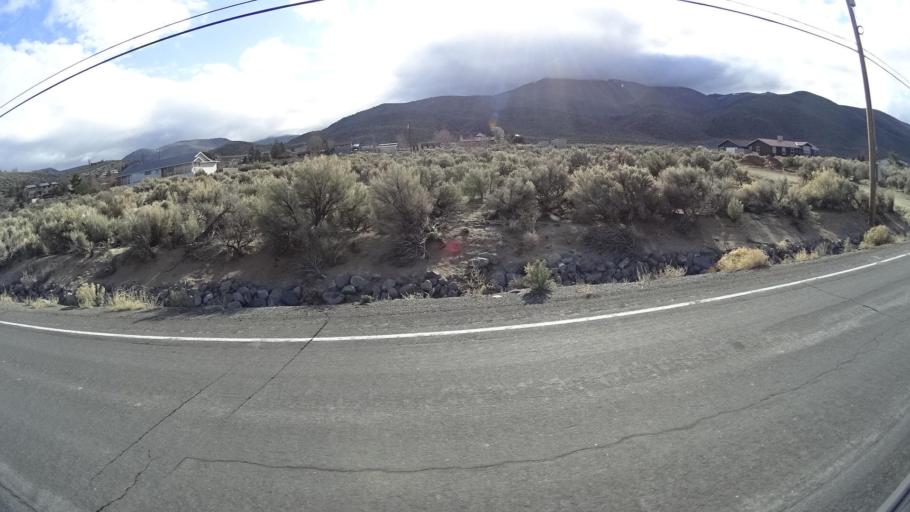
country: US
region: Nevada
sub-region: Storey County
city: Virginia City
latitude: 39.2764
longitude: -119.7567
